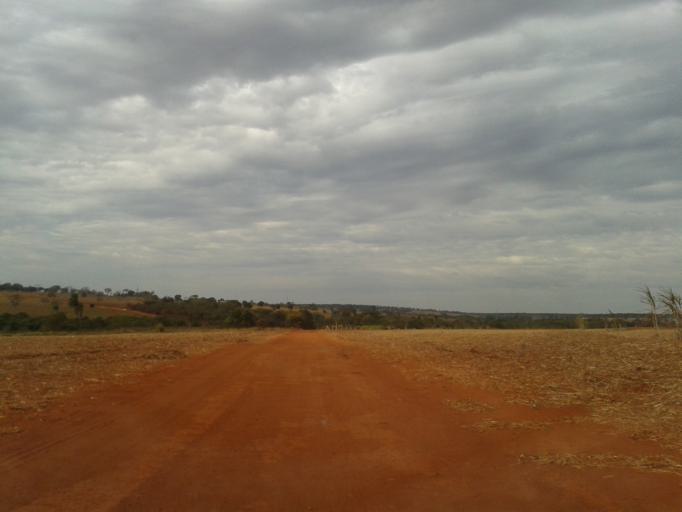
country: BR
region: Minas Gerais
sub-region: Santa Vitoria
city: Santa Vitoria
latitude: -18.7858
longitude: -50.1827
